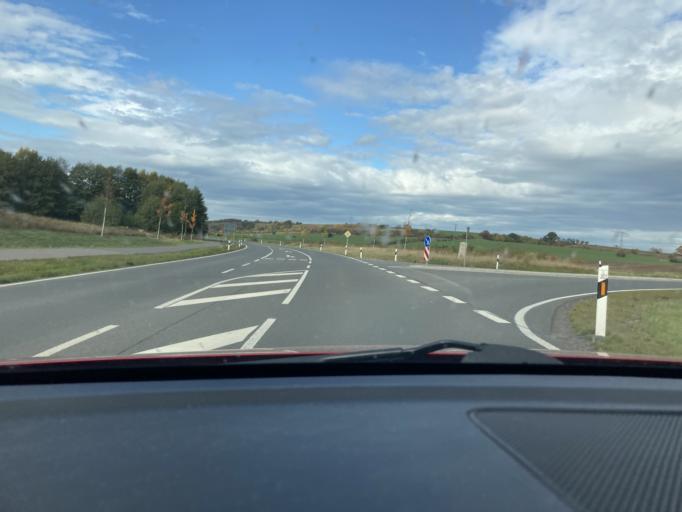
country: DE
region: Thuringia
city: Kleinbodungen
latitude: 51.4686
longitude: 10.5466
